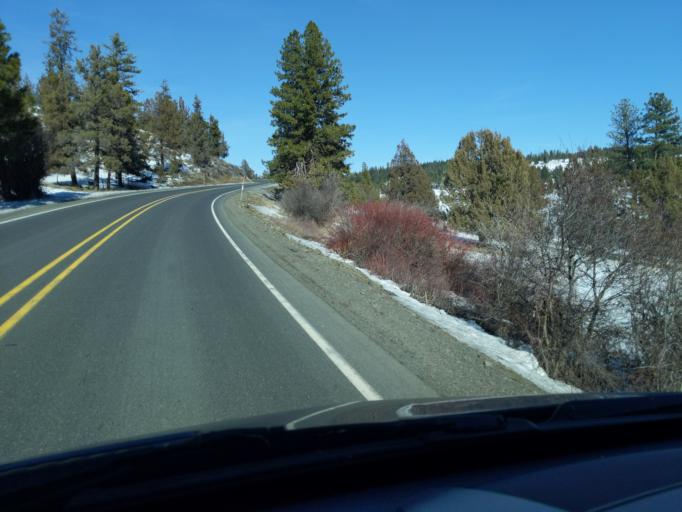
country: US
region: Oregon
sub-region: Grant County
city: John Day
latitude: 44.9034
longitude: -119.0129
